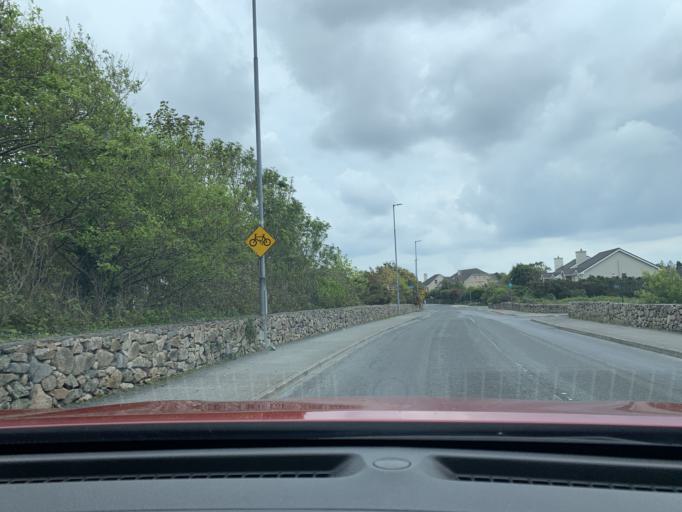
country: IE
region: Connaught
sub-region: County Galway
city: Gaillimh
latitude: 53.2760
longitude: -9.0919
